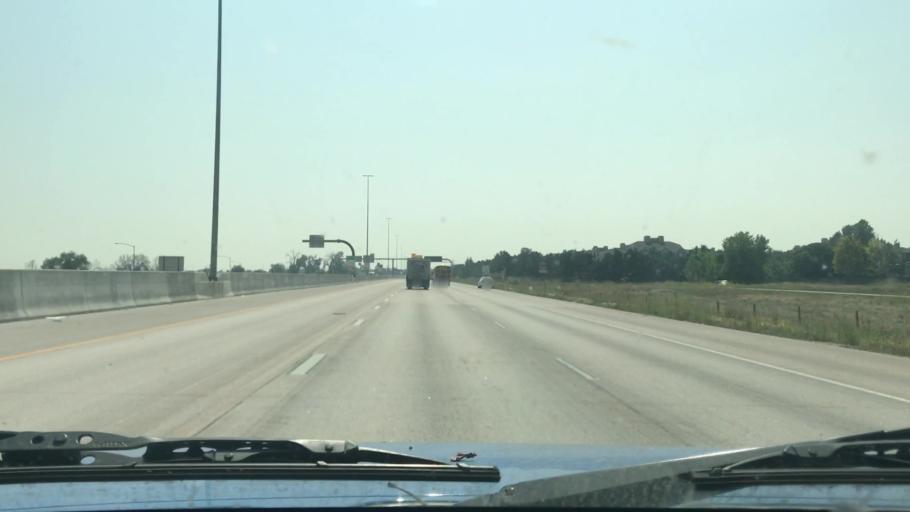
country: US
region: Colorado
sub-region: Broomfield County
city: Broomfield
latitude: 39.8800
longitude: -105.0667
